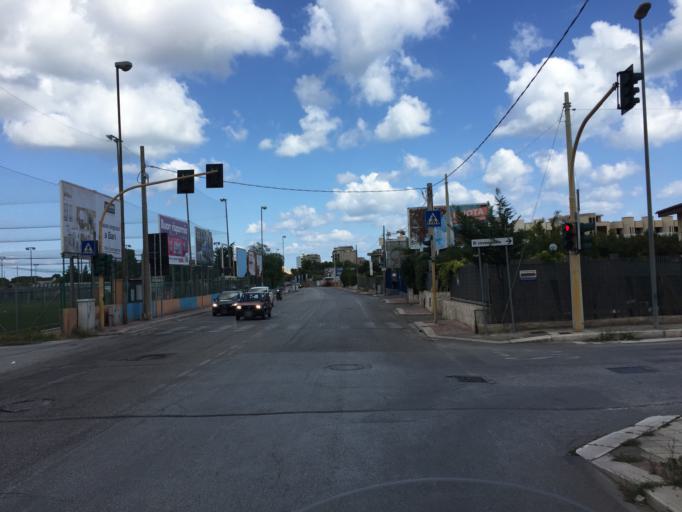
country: IT
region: Apulia
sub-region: Provincia di Bari
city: Bari
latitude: 41.0902
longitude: 16.8837
